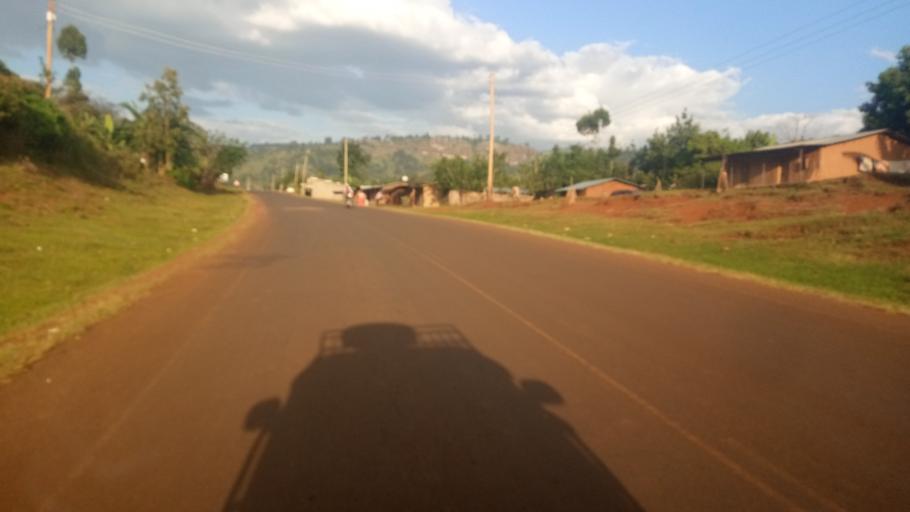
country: UG
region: Eastern Region
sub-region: Kapchorwa District
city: Kapchorwa
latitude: 1.3235
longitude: 34.3506
